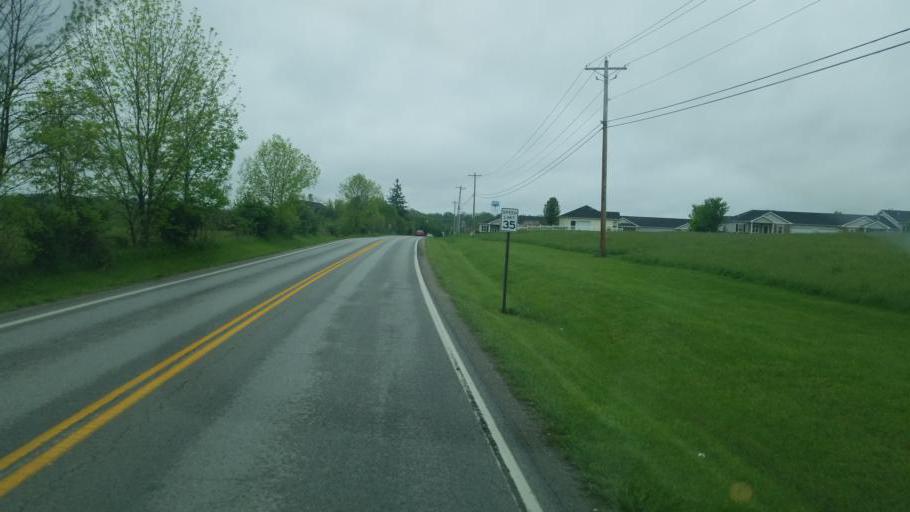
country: US
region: Ohio
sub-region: Highland County
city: Hillsboro
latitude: 39.2212
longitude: -83.6198
